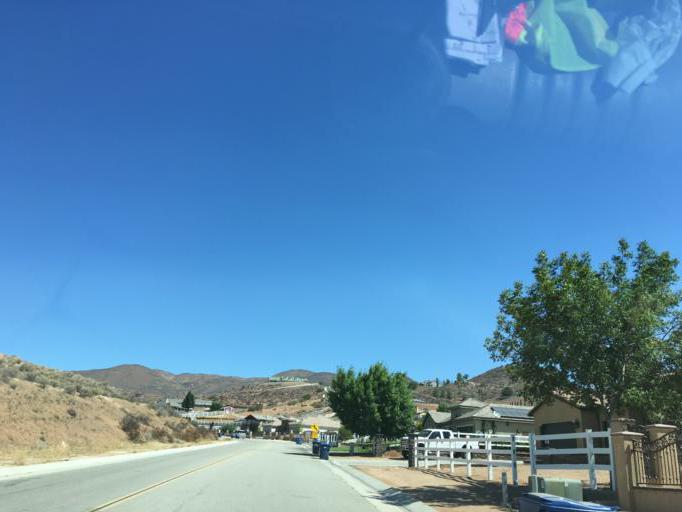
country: US
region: California
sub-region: Los Angeles County
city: Acton
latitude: 34.4928
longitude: -118.1641
